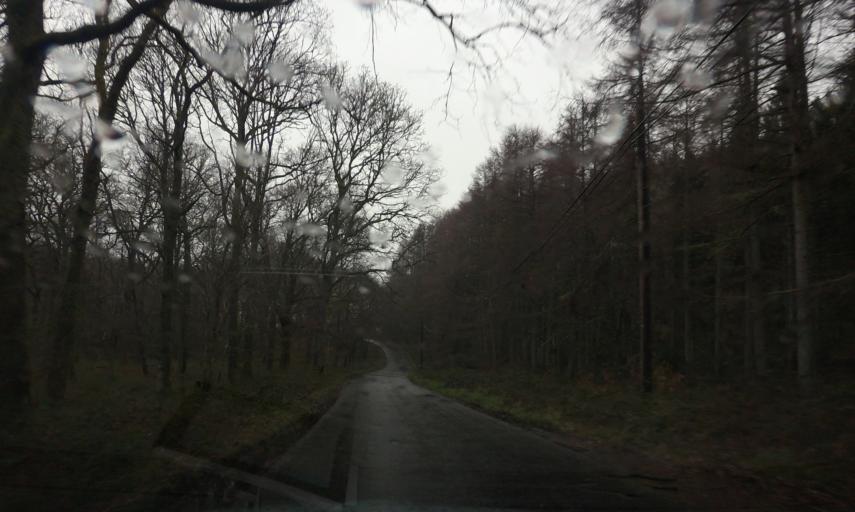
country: GB
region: Scotland
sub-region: West Dunbartonshire
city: Balloch
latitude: 56.1287
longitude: -4.6077
